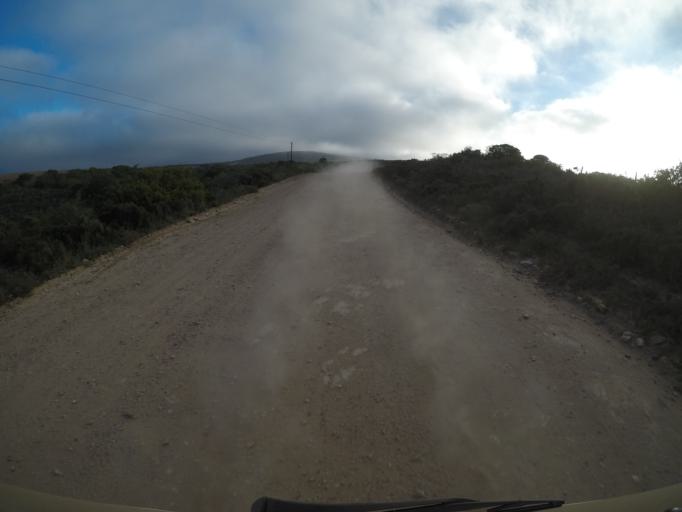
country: ZA
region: Western Cape
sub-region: Eden District Municipality
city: Mossel Bay
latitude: -34.1343
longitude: 22.0426
